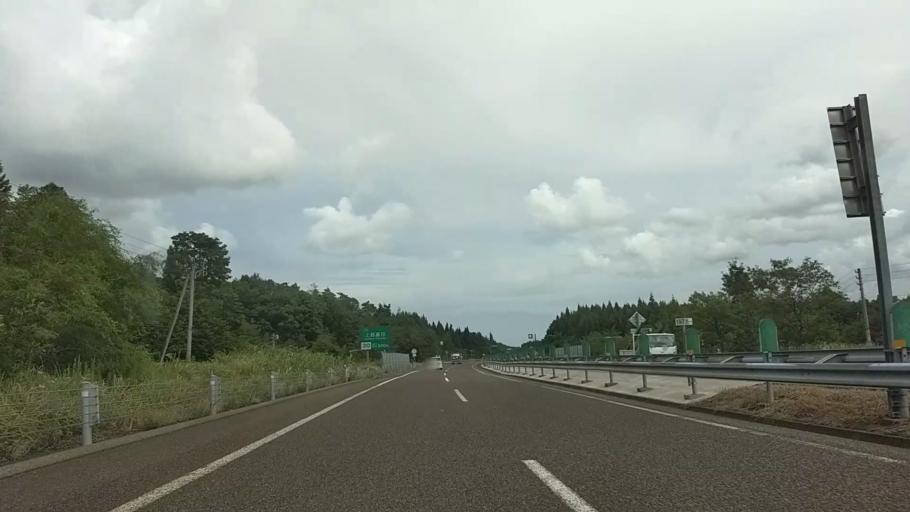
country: JP
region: Niigata
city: Joetsu
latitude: 37.0781
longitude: 138.2241
